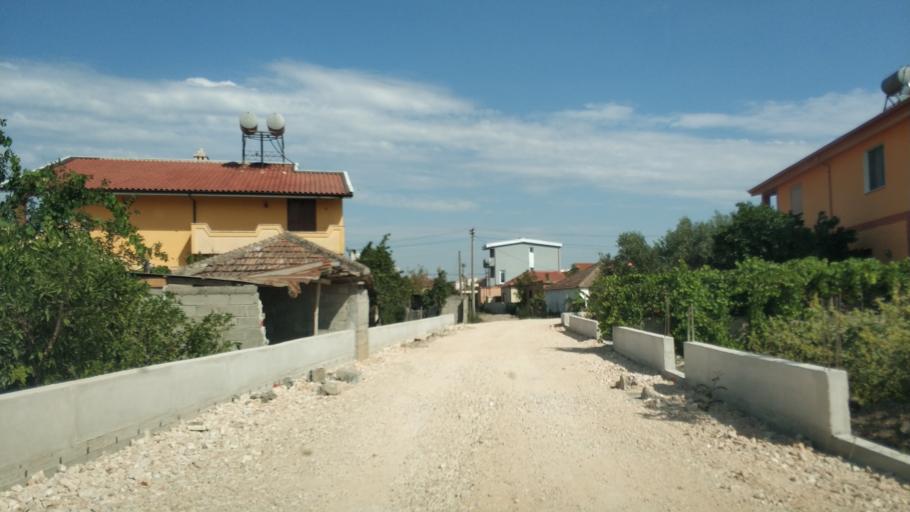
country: AL
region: Fier
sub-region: Rrethi i Lushnjes
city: Divjake
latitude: 40.9941
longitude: 19.5276
